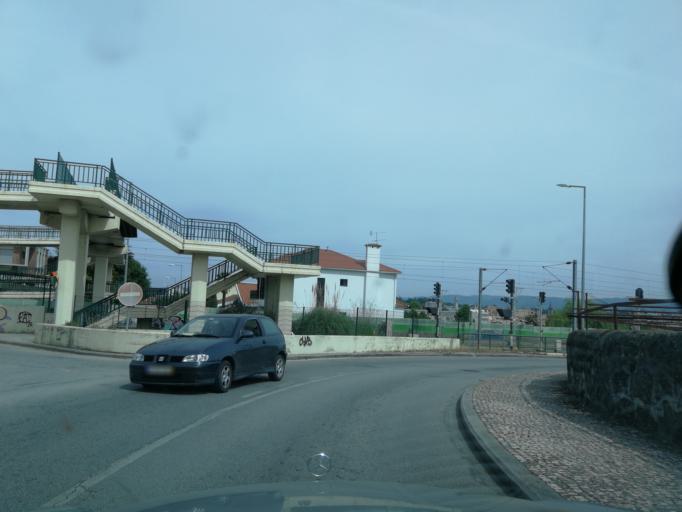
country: PT
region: Braga
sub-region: Vila Nova de Famalicao
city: Vila Nova de Famalicao
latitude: 41.4136
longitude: -8.5267
